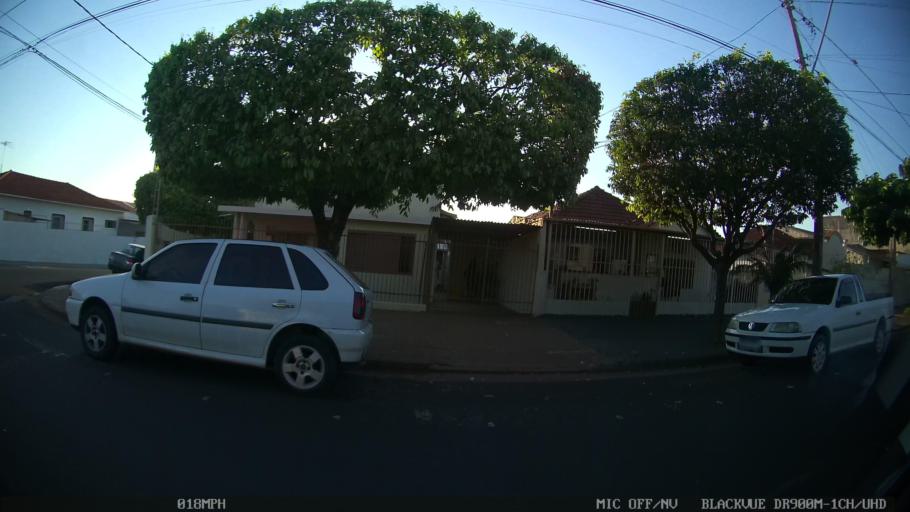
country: BR
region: Sao Paulo
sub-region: Sao Jose Do Rio Preto
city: Sao Jose do Rio Preto
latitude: -20.7964
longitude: -49.3717
